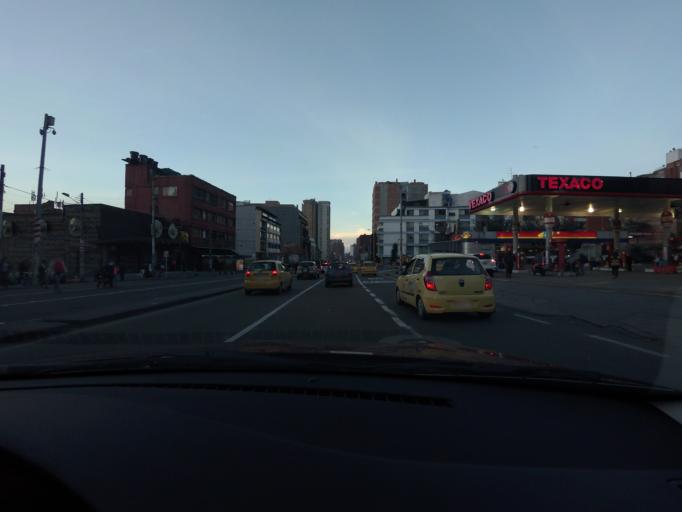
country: CO
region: Bogota D.C.
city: Bogota
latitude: 4.6374
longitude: -74.0634
